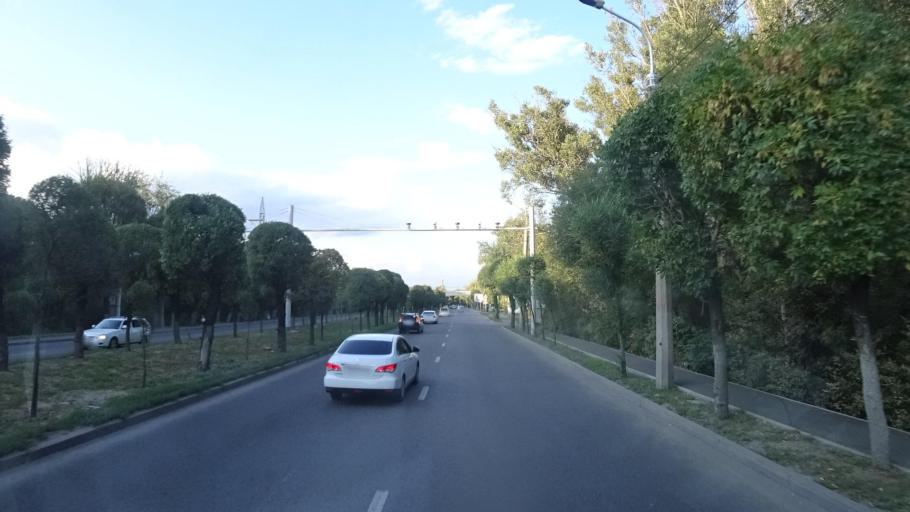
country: KZ
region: Almaty Oblysy
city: Pervomayskiy
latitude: 43.3292
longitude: 76.9770
